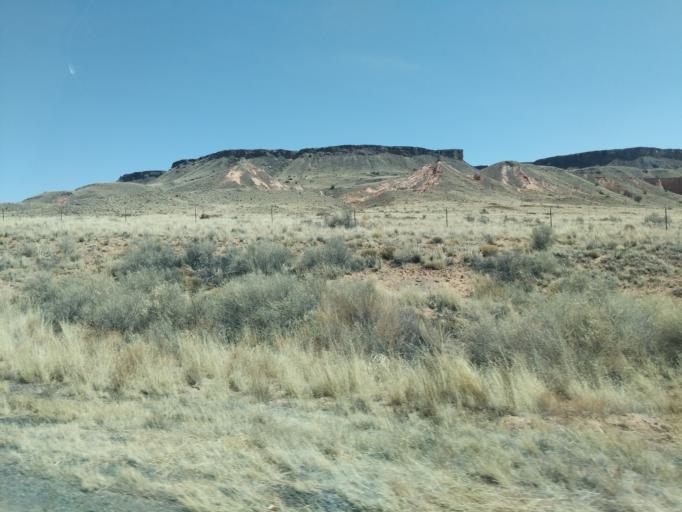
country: US
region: Arizona
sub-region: Navajo County
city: Dilkon
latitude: 35.4352
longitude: -110.0658
